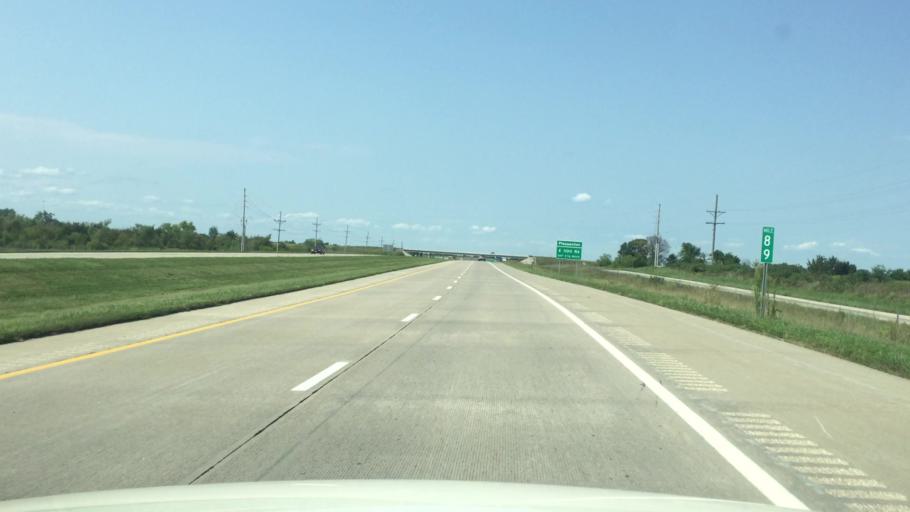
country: US
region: Kansas
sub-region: Linn County
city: Pleasanton
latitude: 38.1610
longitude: -94.6957
